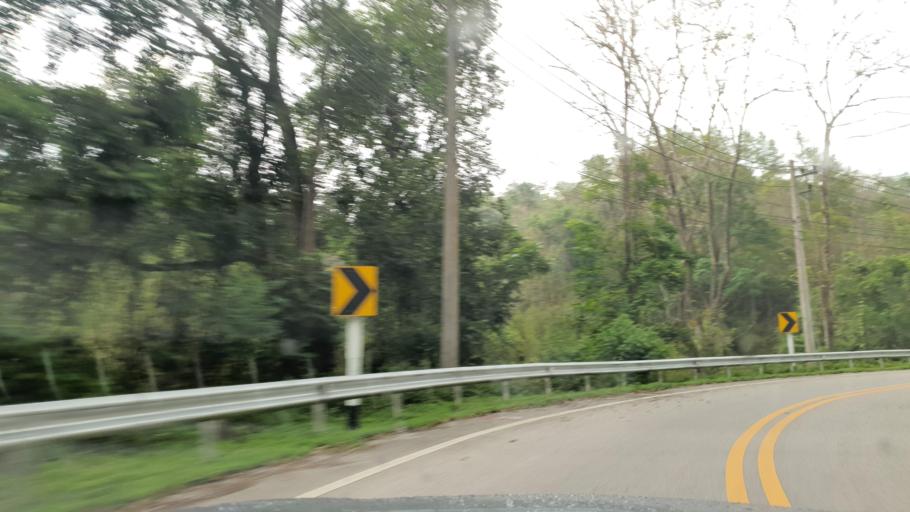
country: TH
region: Chiang Mai
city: Mae Taeng
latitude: 19.1944
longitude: 98.6876
